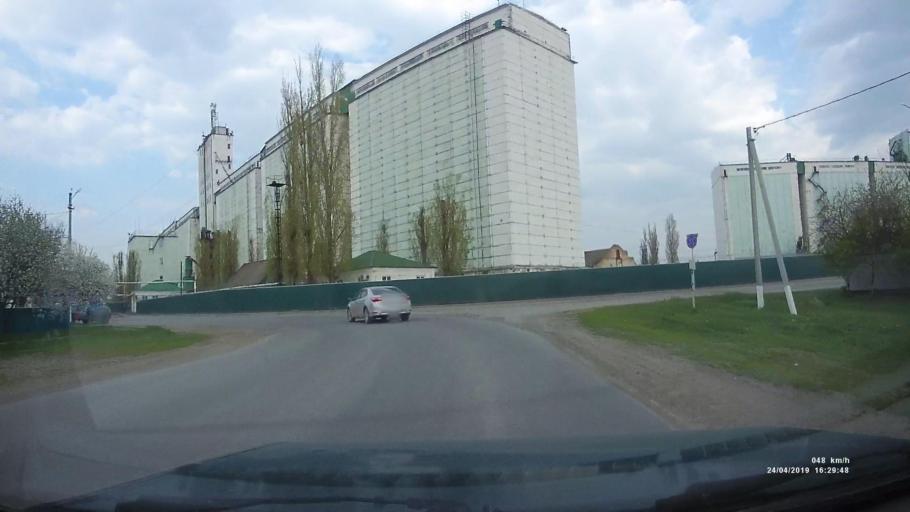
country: RU
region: Rostov
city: Orlovskiy
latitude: 46.8706
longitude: 42.0379
